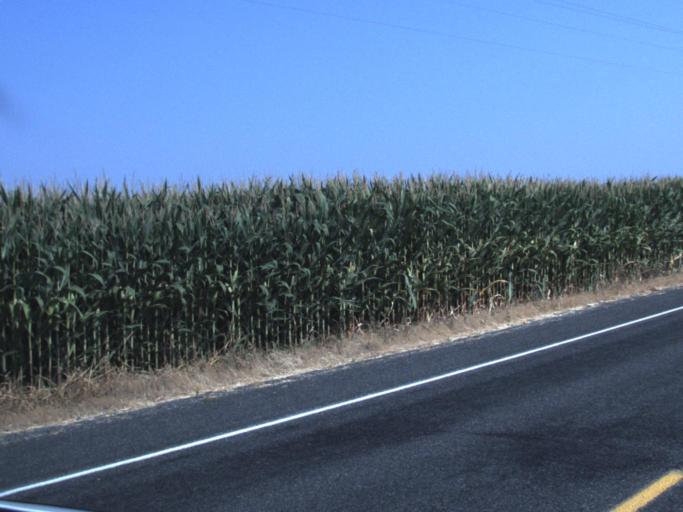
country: US
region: Washington
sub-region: Yakima County
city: Mabton
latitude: 46.2418
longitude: -120.0999
